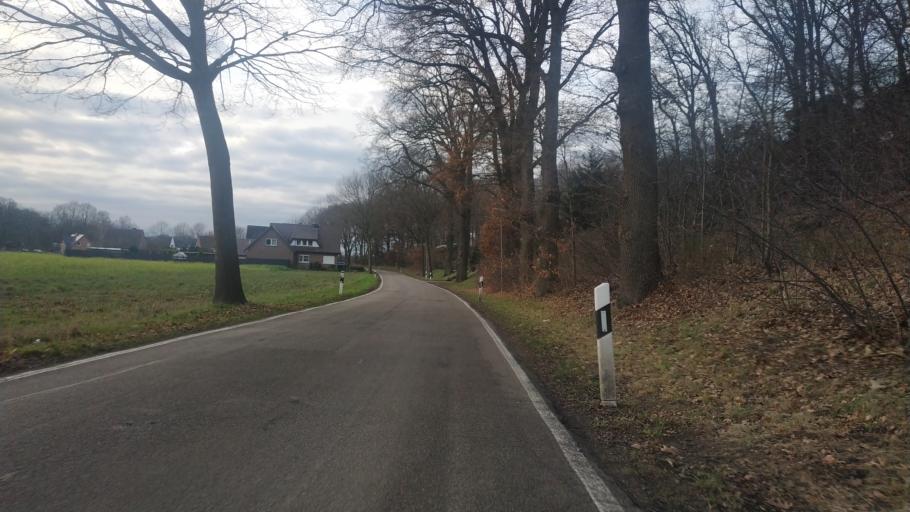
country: DE
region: North Rhine-Westphalia
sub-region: Regierungsbezirk Munster
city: Horstel
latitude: 52.2795
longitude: 7.5973
